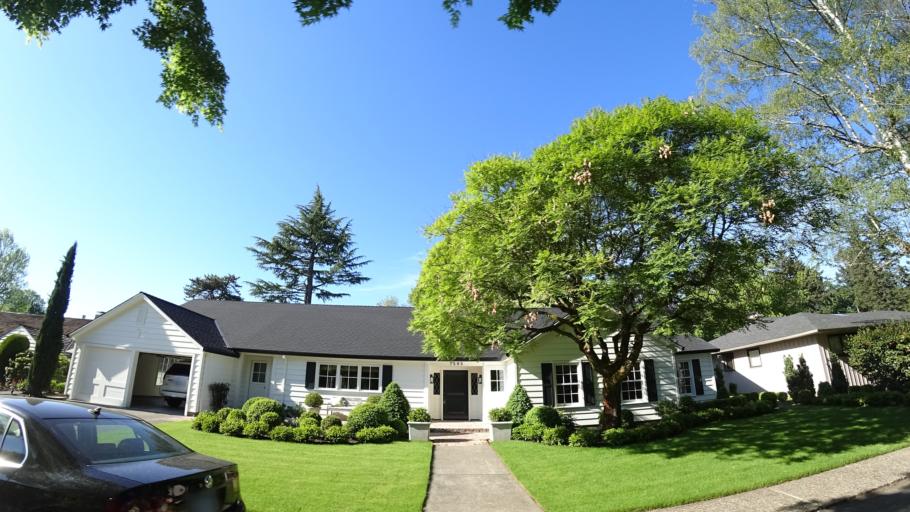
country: US
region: Oregon
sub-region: Washington County
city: Raleigh Hills
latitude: 45.4893
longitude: -122.7552
